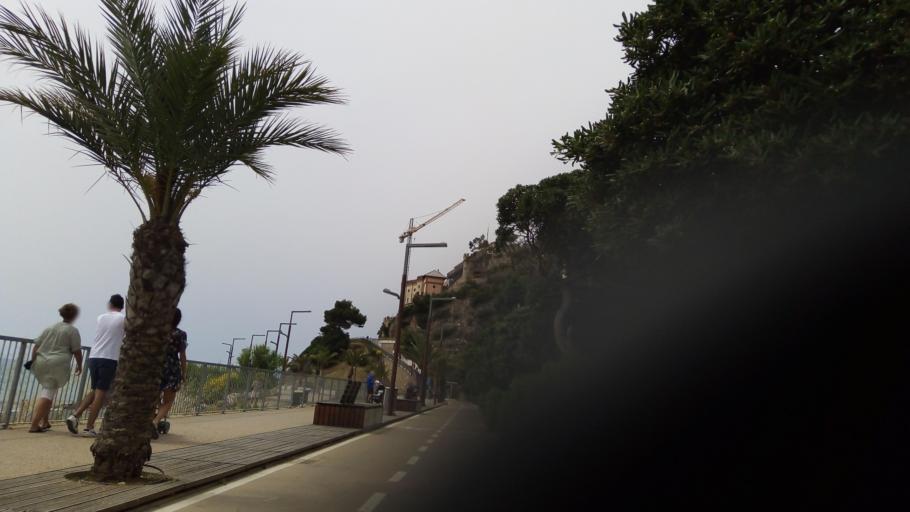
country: IT
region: Liguria
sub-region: Provincia di Savona
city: Borghetto Santo Spirito
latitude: 44.1059
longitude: 8.2398
